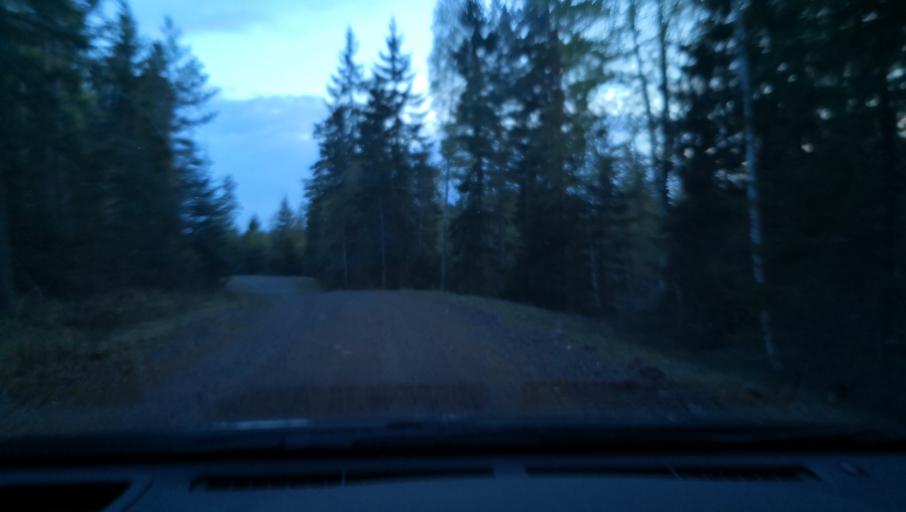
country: SE
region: OErebro
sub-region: Askersunds Kommun
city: Asbro
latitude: 59.0019
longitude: 14.9317
